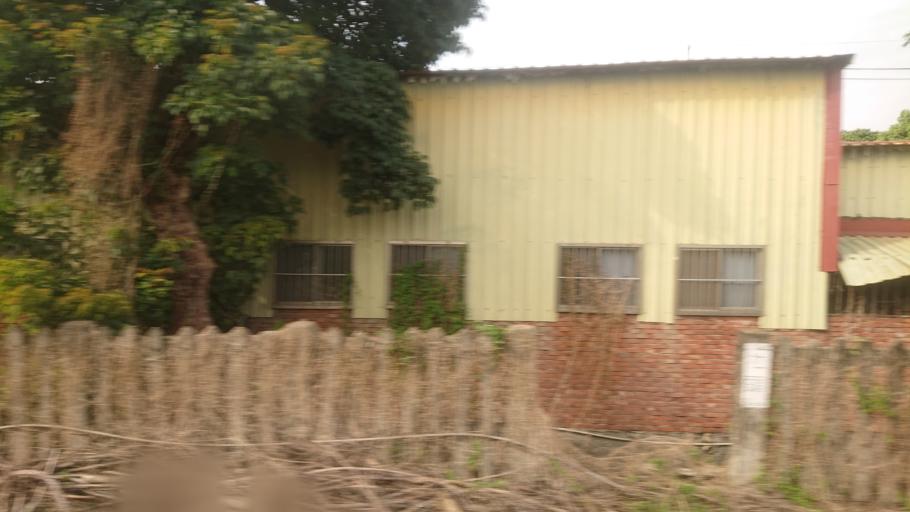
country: TW
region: Taiwan
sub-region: Nantou
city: Nantou
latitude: 23.8971
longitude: 120.5802
